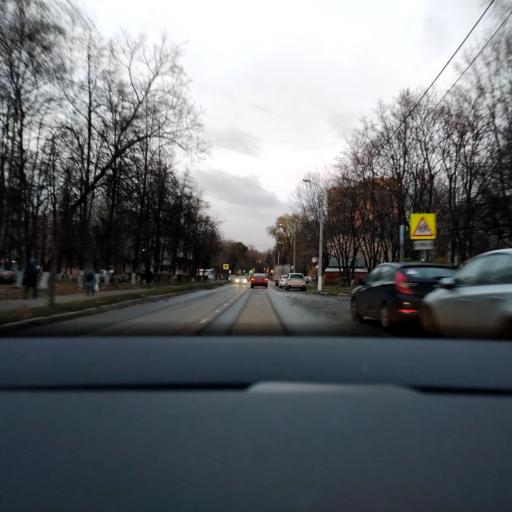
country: RU
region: Moskovskaya
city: Reutov
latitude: 55.7617
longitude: 37.8628
